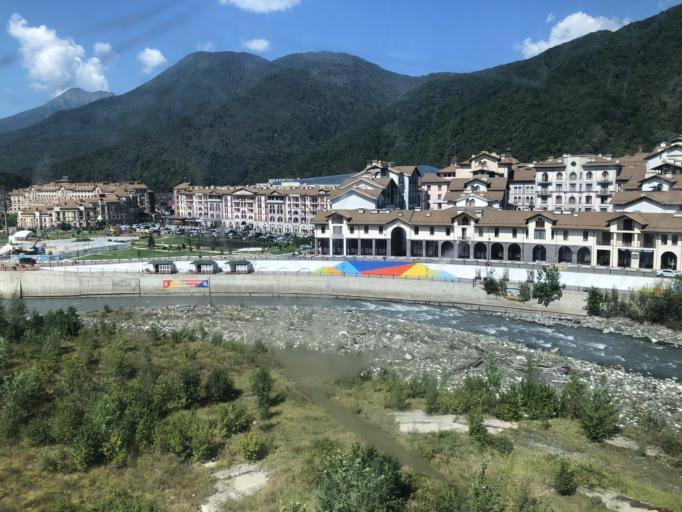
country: RU
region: Krasnodarskiy
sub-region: Sochi City
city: Krasnaya Polyana
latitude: 43.6817
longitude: 40.2660
